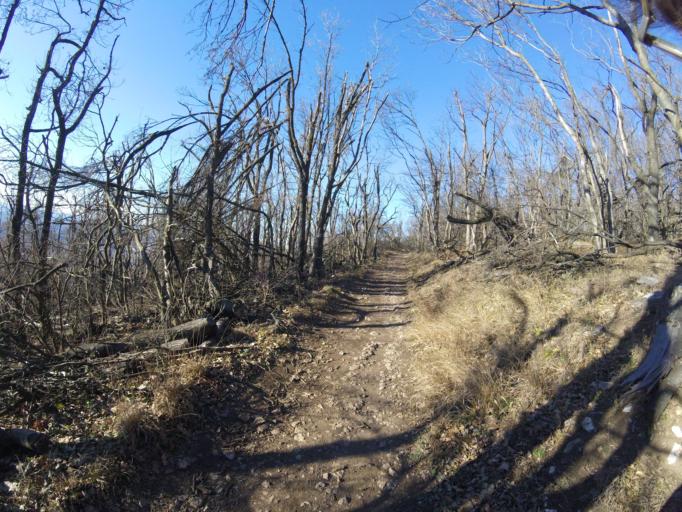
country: HU
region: Pest
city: Pilisszanto
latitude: 47.6846
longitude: 18.8725
